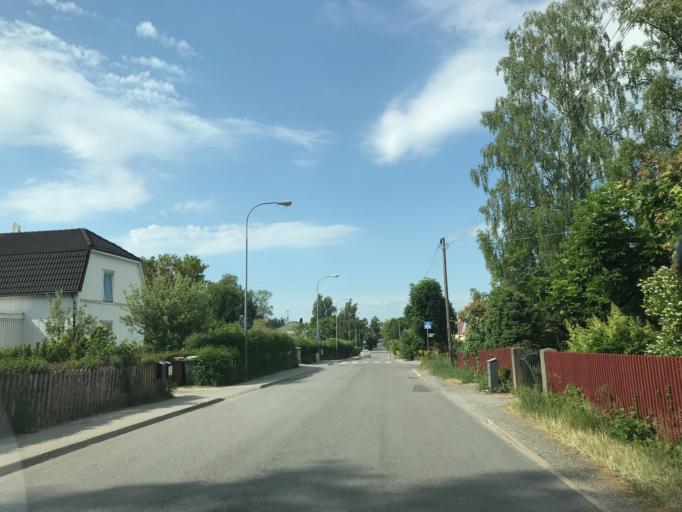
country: SE
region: Stockholm
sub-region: Sollentuna Kommun
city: Sollentuna
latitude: 59.4132
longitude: 17.9607
